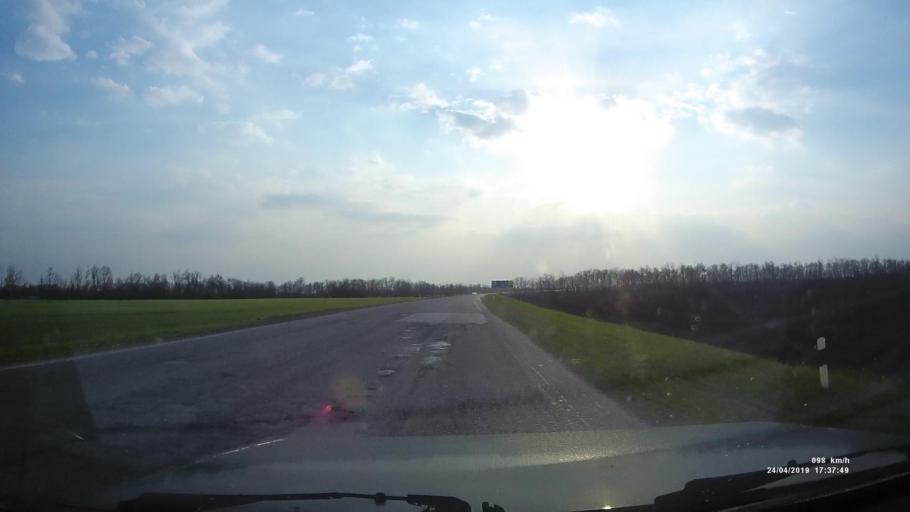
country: RU
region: Rostov
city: Tselina
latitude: 46.5116
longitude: 41.0191
